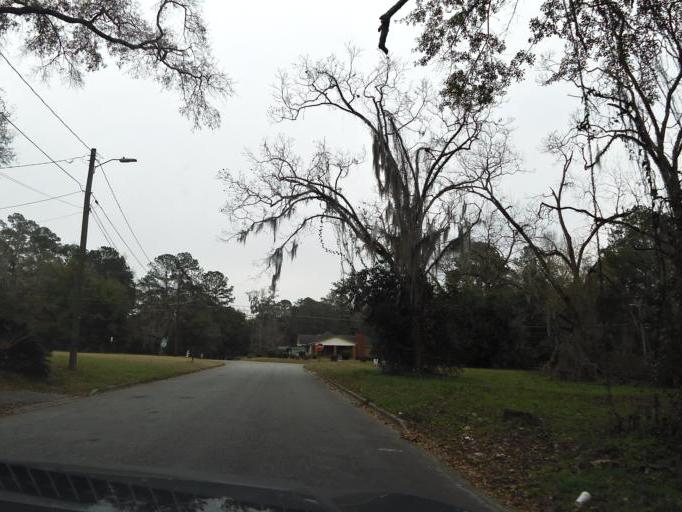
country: US
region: Georgia
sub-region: Thomas County
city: Thomasville
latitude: 30.8224
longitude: -83.9783
